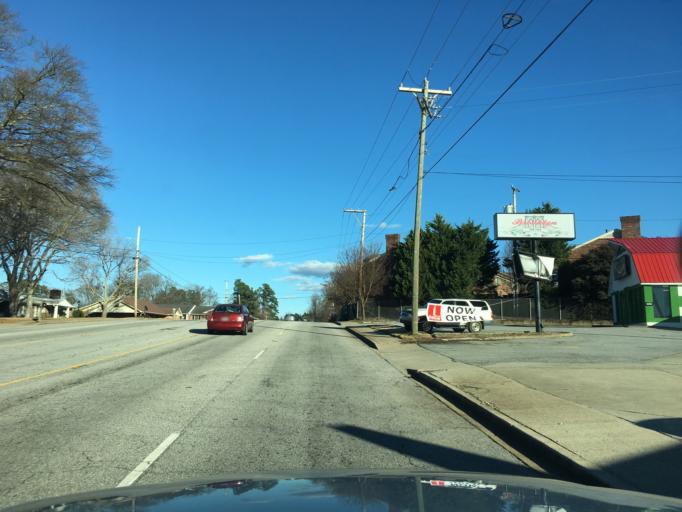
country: US
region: South Carolina
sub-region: Greenville County
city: Wade Hampton
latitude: 34.8693
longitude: -82.3533
